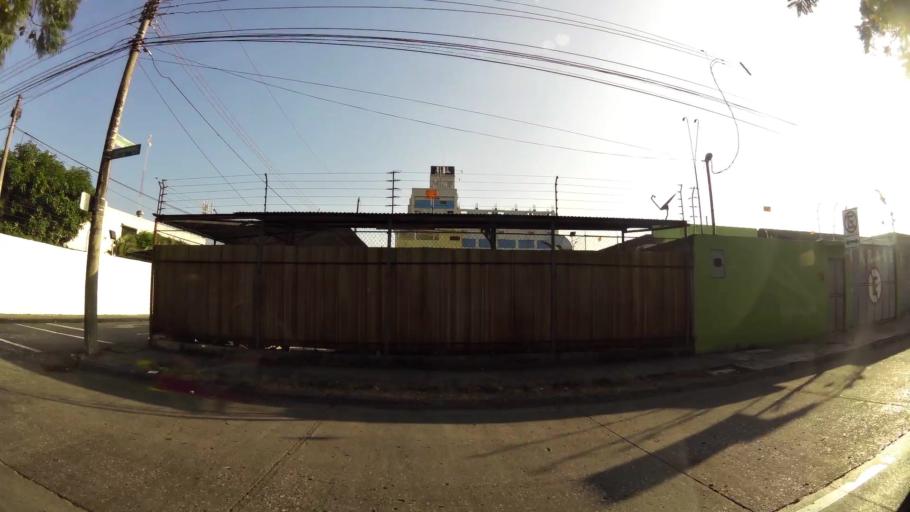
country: EC
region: Guayas
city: Eloy Alfaro
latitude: -2.1657
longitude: -79.8935
